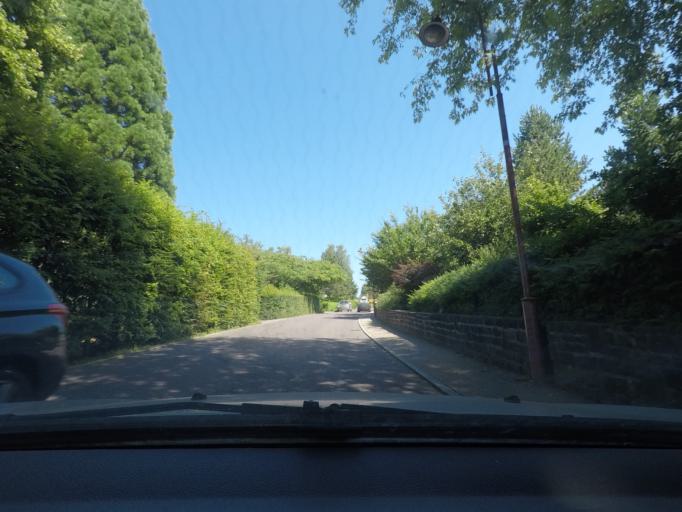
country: LU
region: Diekirch
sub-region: Canton de Redange
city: Redange-sur-Attert
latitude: 49.7666
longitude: 5.8956
